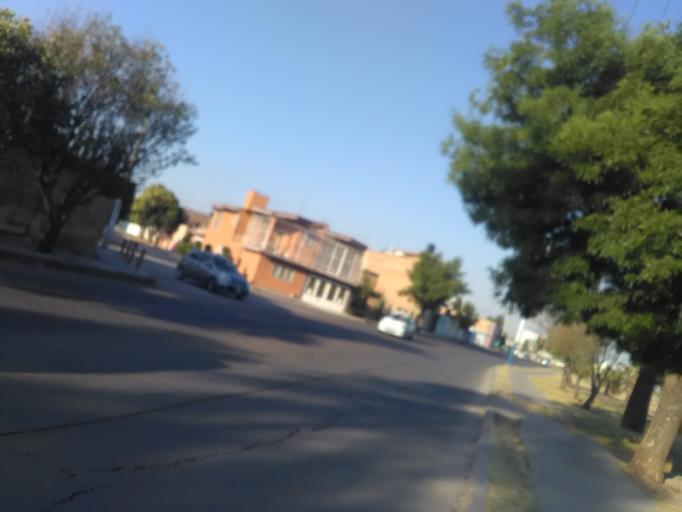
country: MX
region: Durango
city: Victoria de Durango
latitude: 24.0391
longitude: -104.6530
